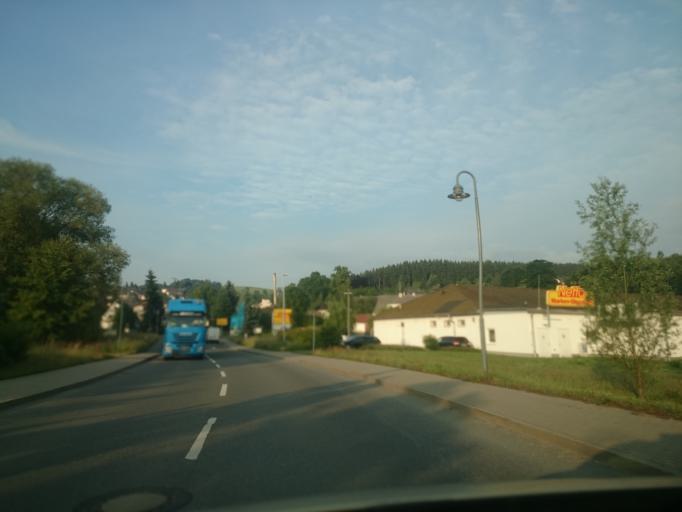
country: DE
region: Saxony
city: Pockau
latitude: 50.7117
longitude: 13.2219
